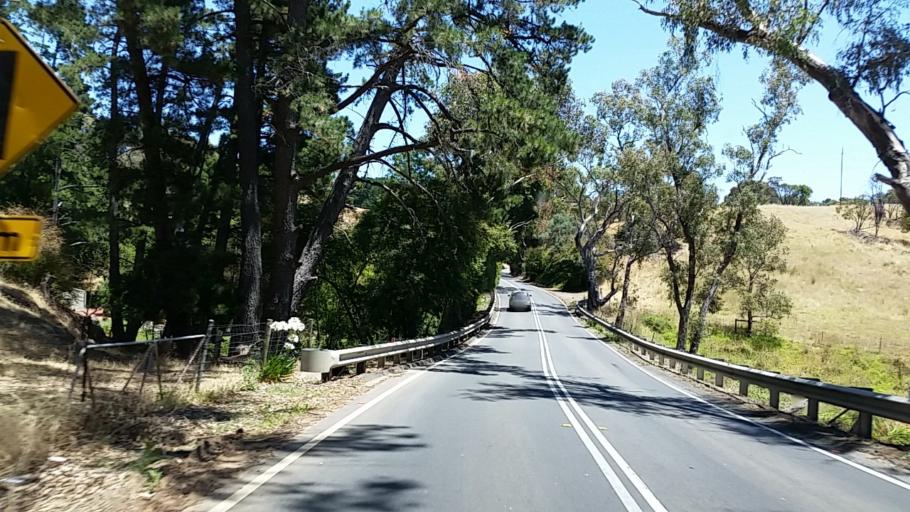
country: AU
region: South Australia
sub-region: Tea Tree Gully
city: Golden Grove
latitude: -34.8246
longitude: 138.7615
